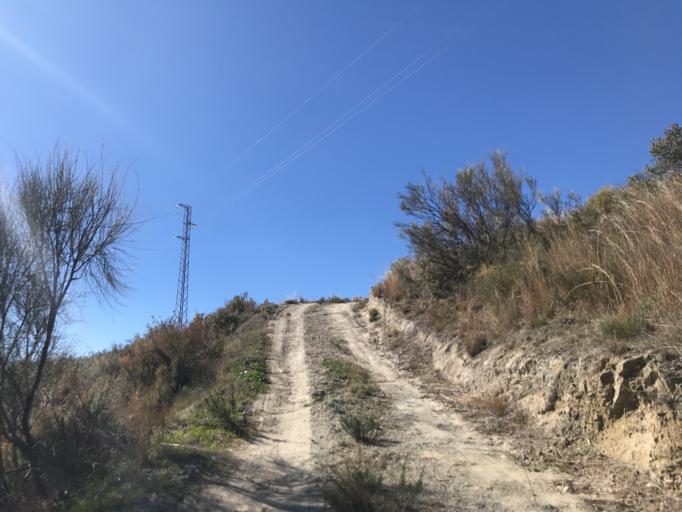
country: ES
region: Andalusia
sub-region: Provincia de Malaga
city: Canillas de Albaida
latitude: 36.8518
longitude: -3.9878
